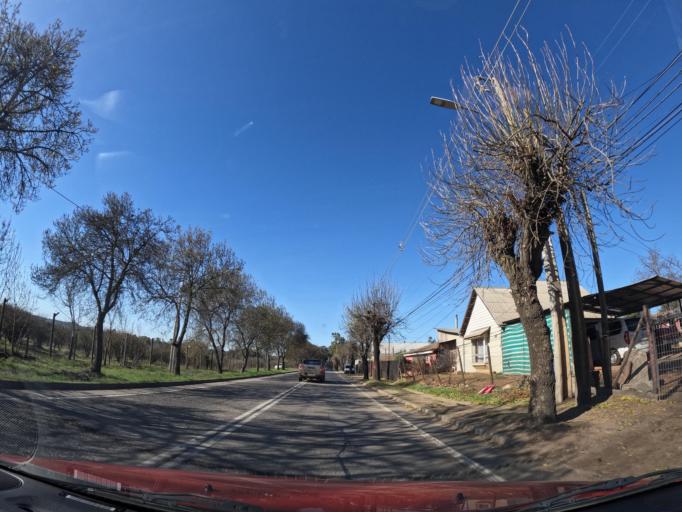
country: CL
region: Maule
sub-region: Provincia de Cauquenes
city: Cauquenes
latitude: -35.9579
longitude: -72.2970
